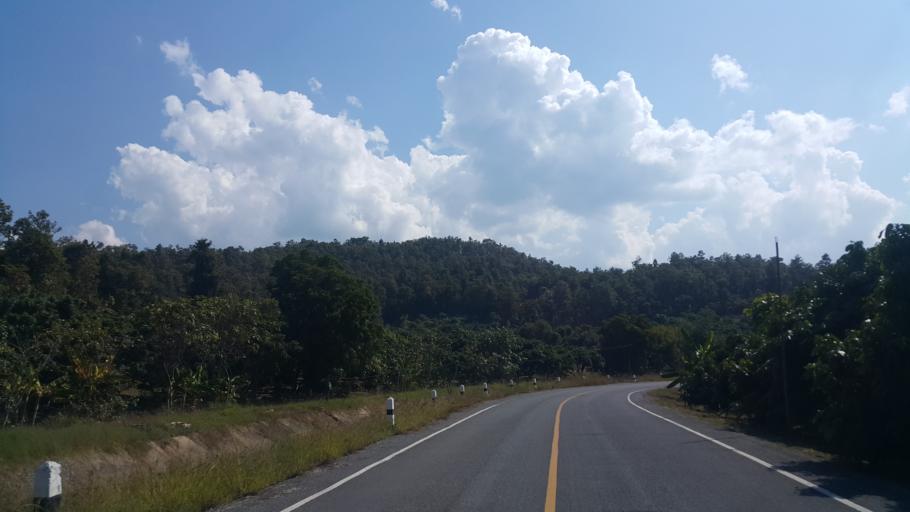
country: TH
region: Lamphun
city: Ban Thi
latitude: 18.6403
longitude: 99.1621
